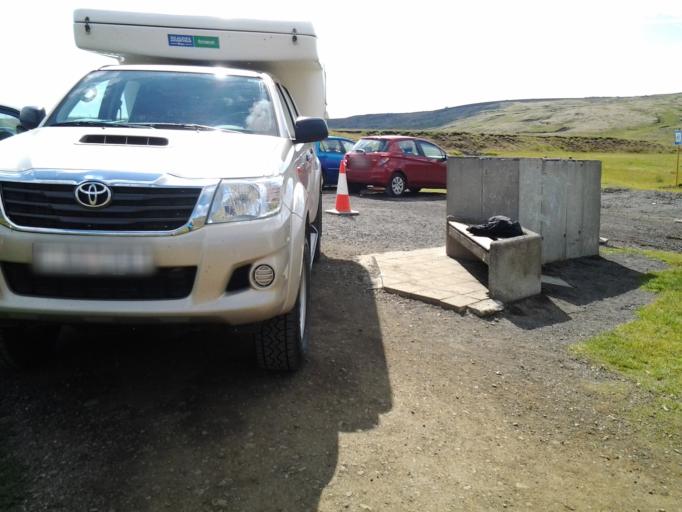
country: IS
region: South
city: Hveragerdi
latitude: 64.0227
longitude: -21.2118
